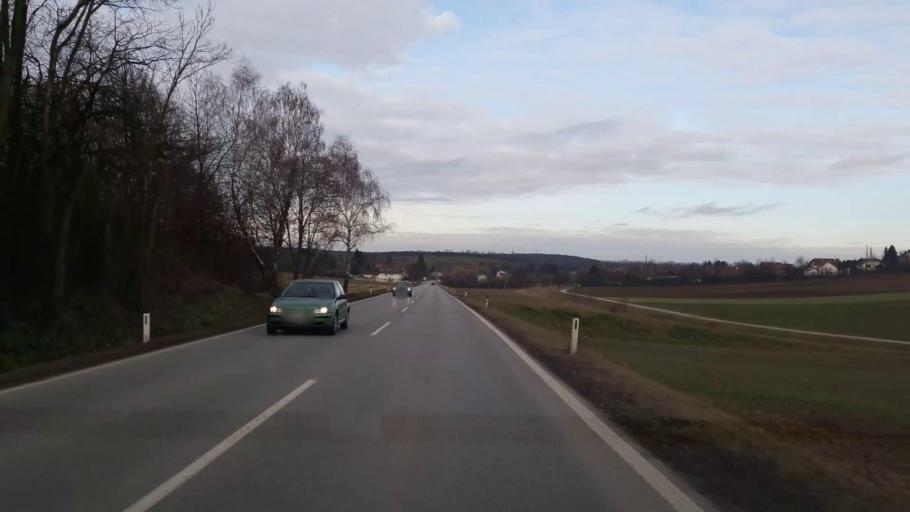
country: AT
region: Lower Austria
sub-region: Politischer Bezirk Mistelbach
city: Asparn an der Zaya
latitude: 48.6179
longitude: 16.5224
